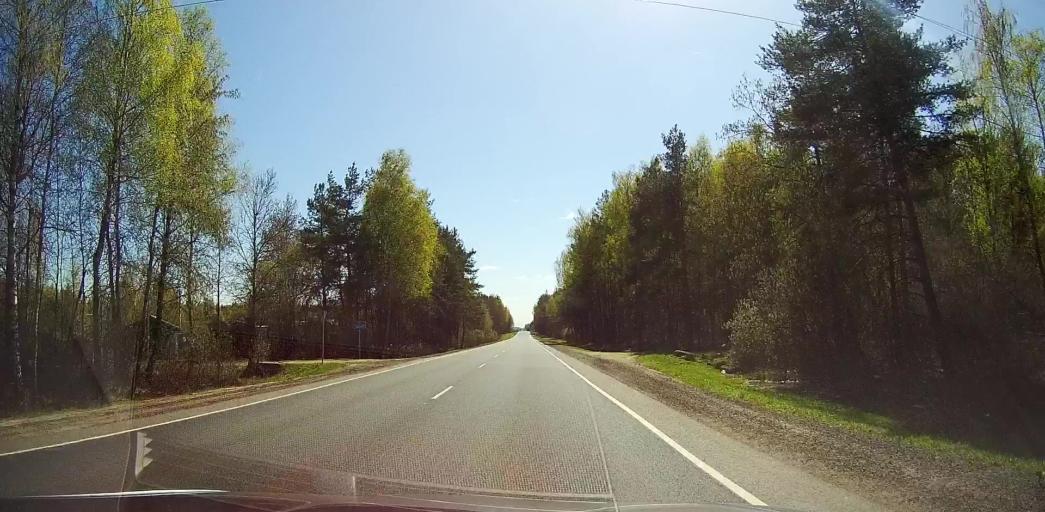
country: RU
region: Moskovskaya
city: Gzhel'
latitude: 55.6050
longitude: 38.3764
